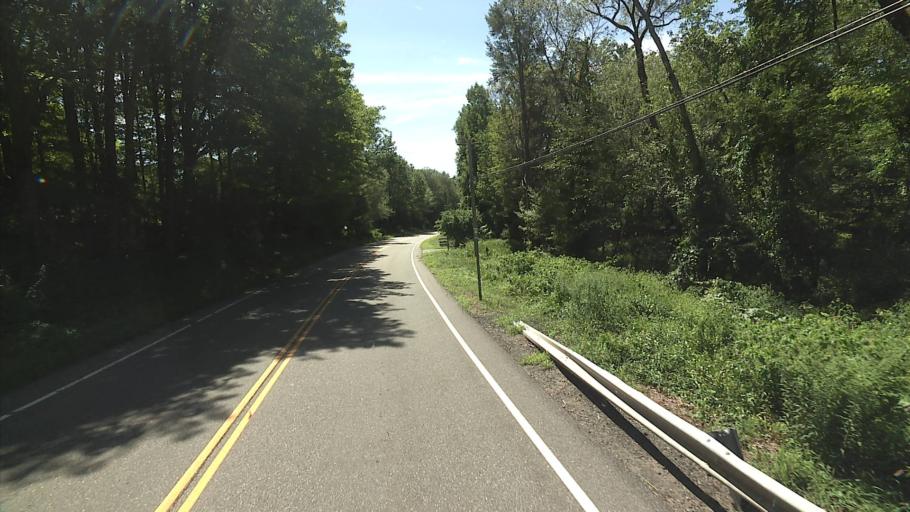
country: US
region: Connecticut
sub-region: Windham County
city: East Brooklyn
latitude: 41.8084
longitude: -72.0470
